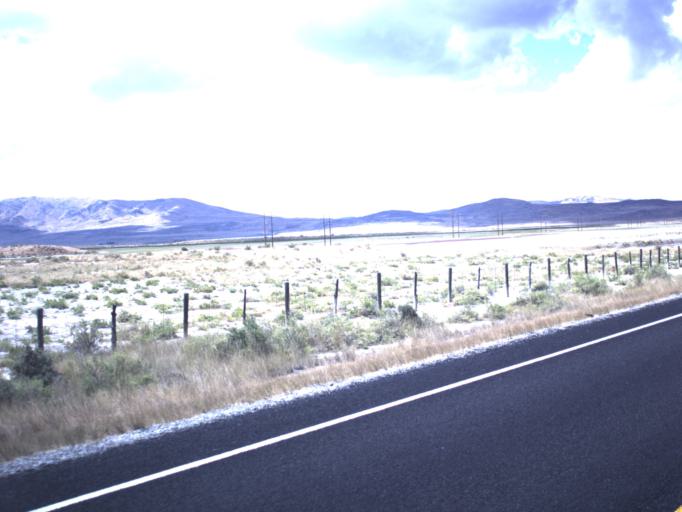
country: US
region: Utah
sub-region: Box Elder County
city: Tremonton
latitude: 41.6217
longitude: -112.3884
